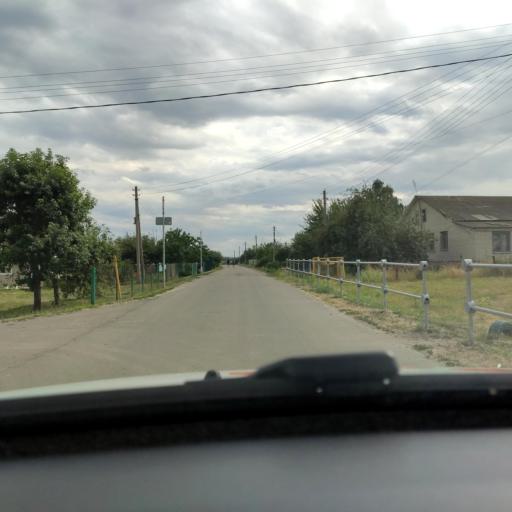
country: RU
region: Voronezj
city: Orlovo
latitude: 51.6543
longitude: 39.5723
